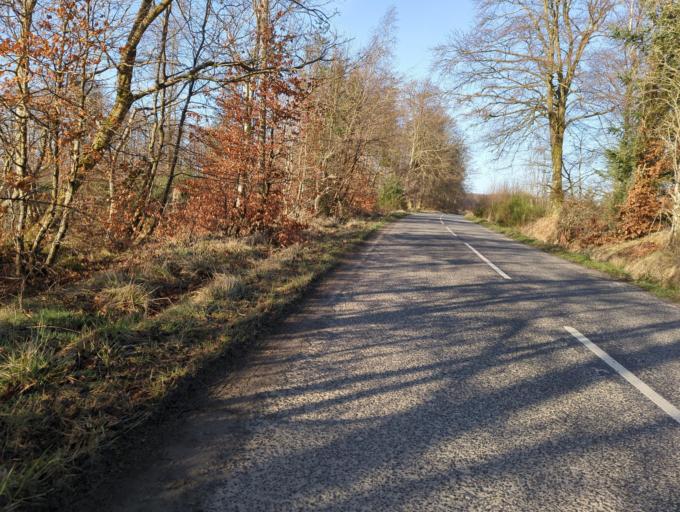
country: GB
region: Scotland
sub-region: Perth and Kinross
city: Methven
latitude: 56.4562
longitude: -3.5730
